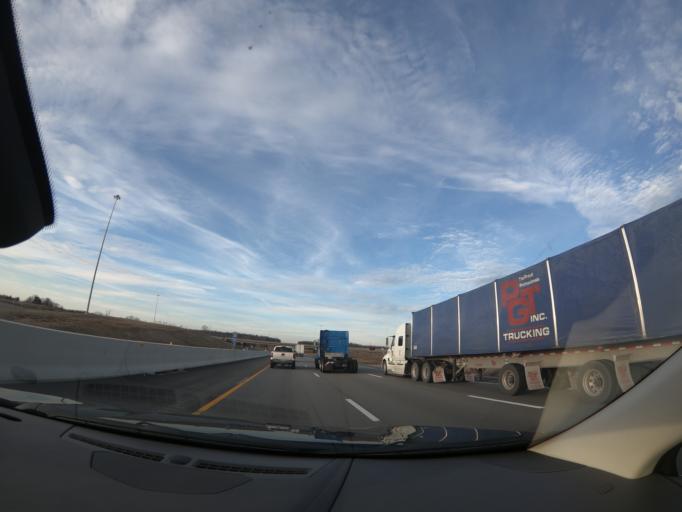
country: US
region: Kentucky
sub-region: Hart County
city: Munfordville
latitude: 37.4565
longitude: -85.8829
